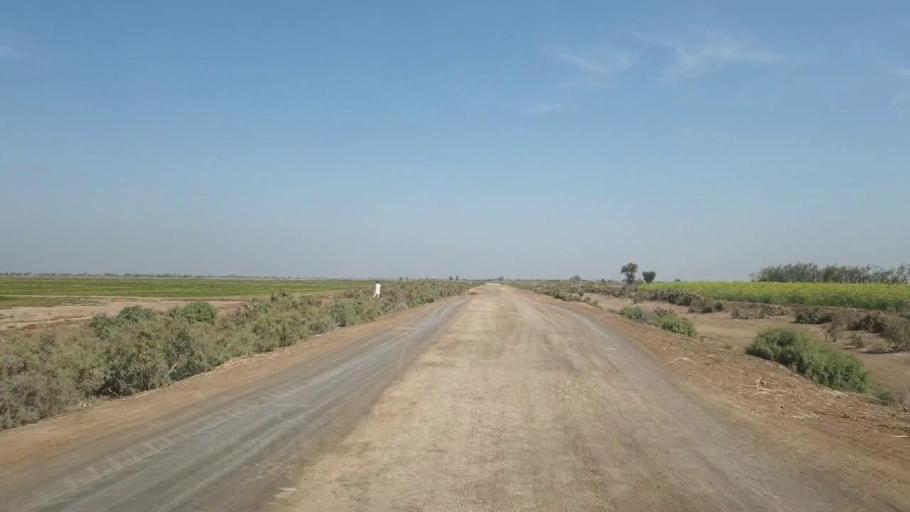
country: PK
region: Sindh
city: Samaro
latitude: 25.3508
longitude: 69.2519
